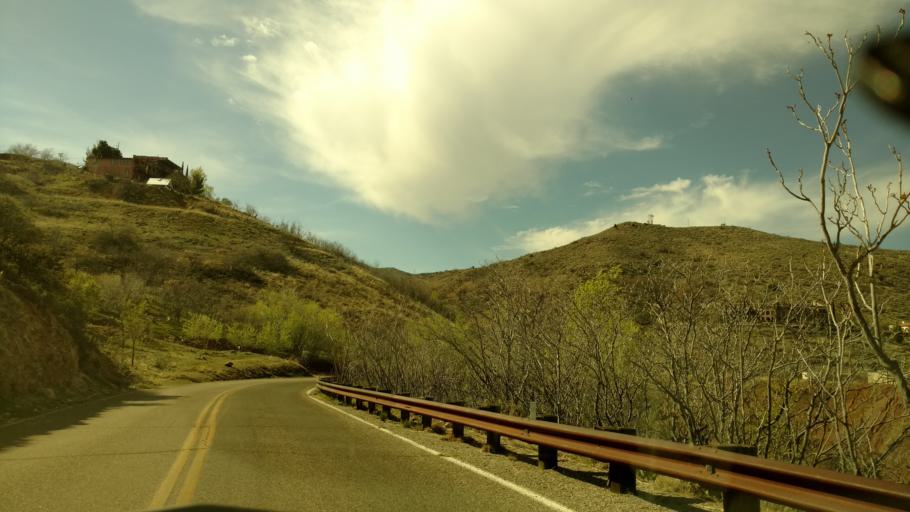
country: US
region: Arizona
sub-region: Yavapai County
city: Clarkdale
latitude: 34.7510
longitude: -112.1118
